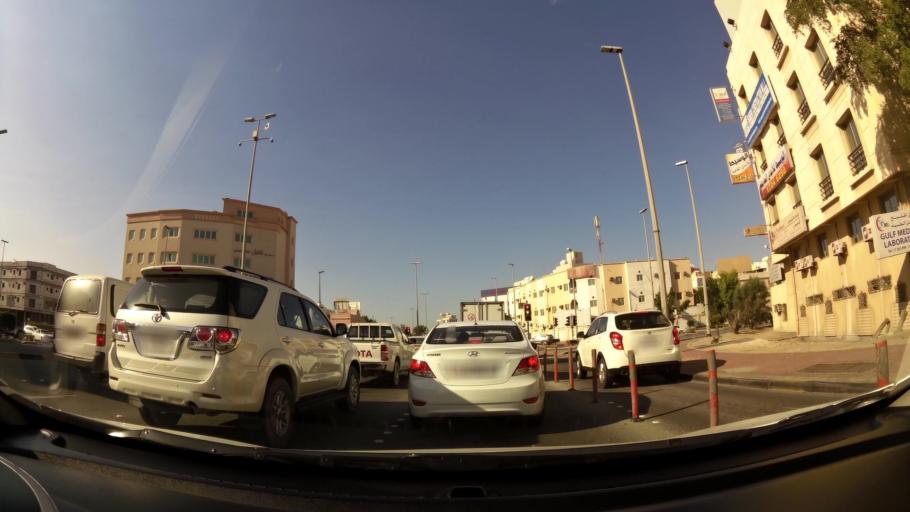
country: BH
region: Manama
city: Manama
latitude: 26.2121
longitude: 50.5661
